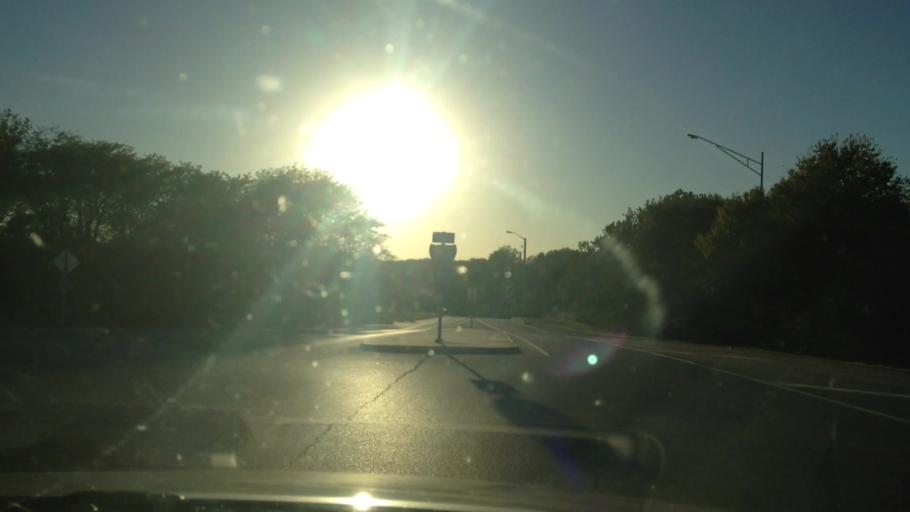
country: US
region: Missouri
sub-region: Clay County
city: Pleasant Valley
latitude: 39.2888
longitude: -94.5124
